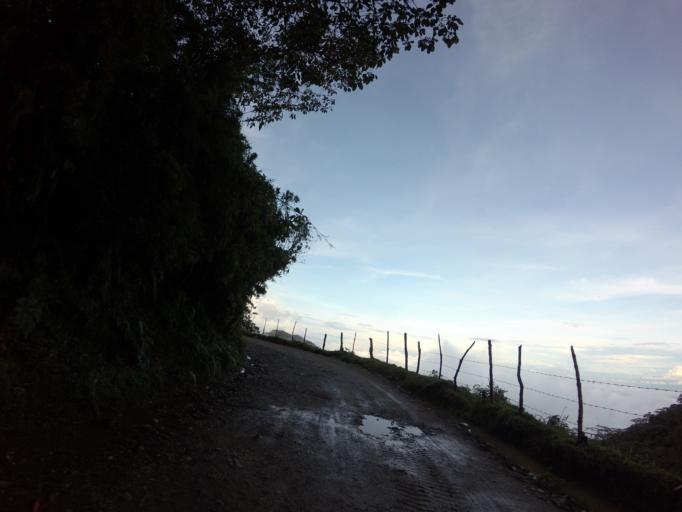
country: CO
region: Caldas
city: Pensilvania
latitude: 5.4295
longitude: -75.1295
